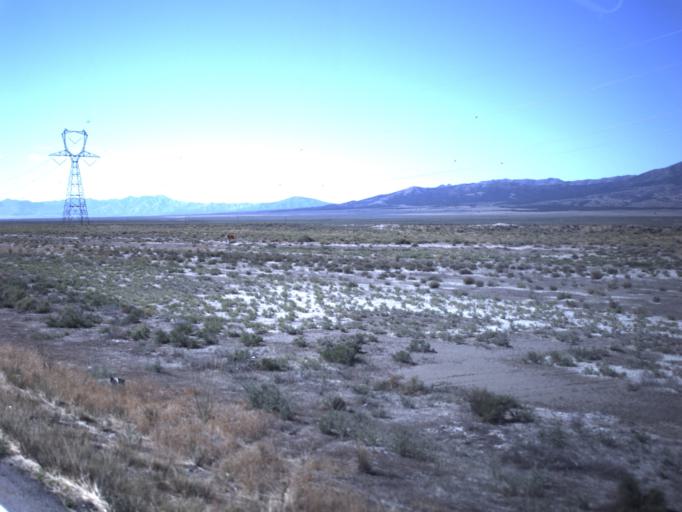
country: US
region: Utah
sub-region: Tooele County
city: Tooele
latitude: 40.3213
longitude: -112.4066
